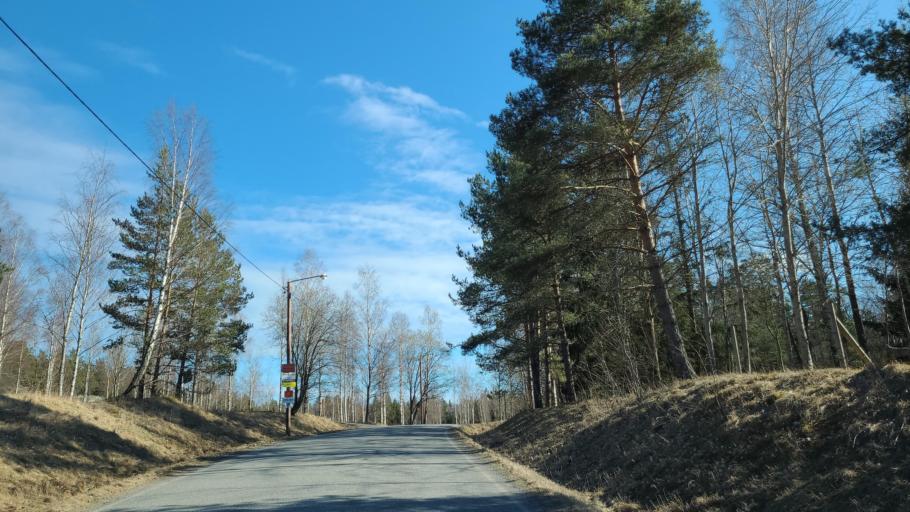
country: SE
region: Stockholm
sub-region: Varmdo Kommun
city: Hemmesta
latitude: 59.2815
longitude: 18.5690
